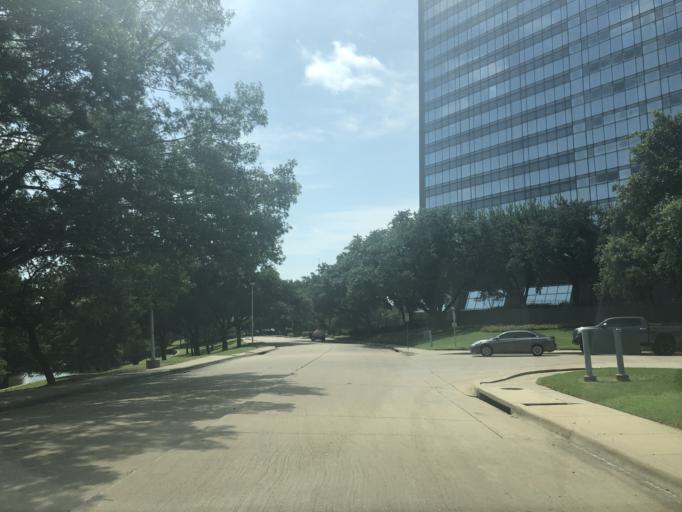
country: US
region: Texas
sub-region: Dallas County
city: Dallas
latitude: 32.8110
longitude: -96.8605
